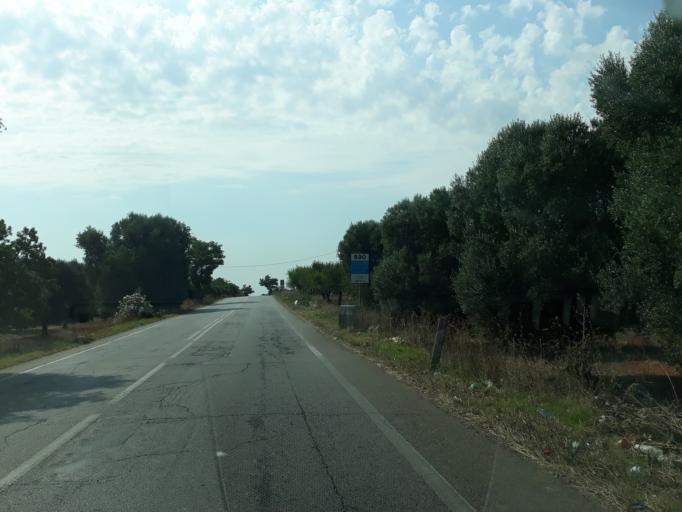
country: IT
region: Apulia
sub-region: Provincia di Brindisi
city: Carovigno
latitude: 40.6932
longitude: 17.6712
